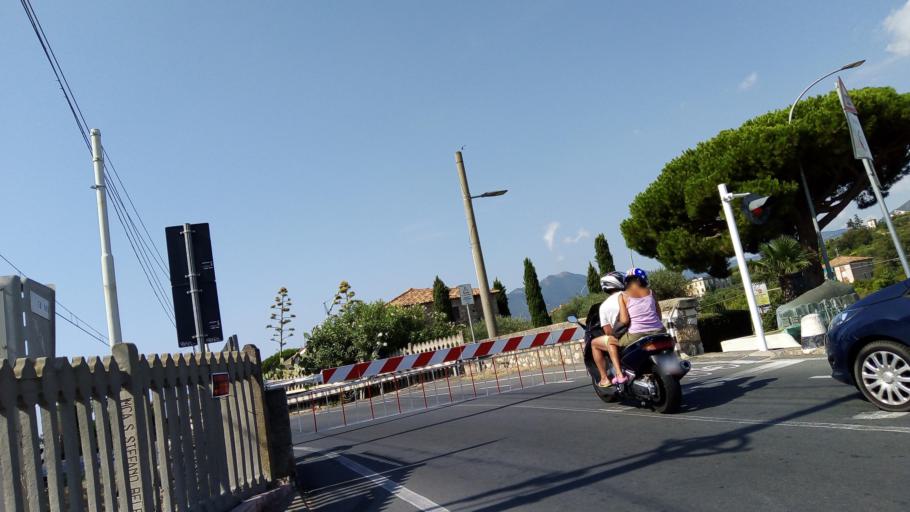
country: IT
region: Liguria
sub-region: Provincia di Savona
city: Loano
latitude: 44.1372
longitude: 8.2668
